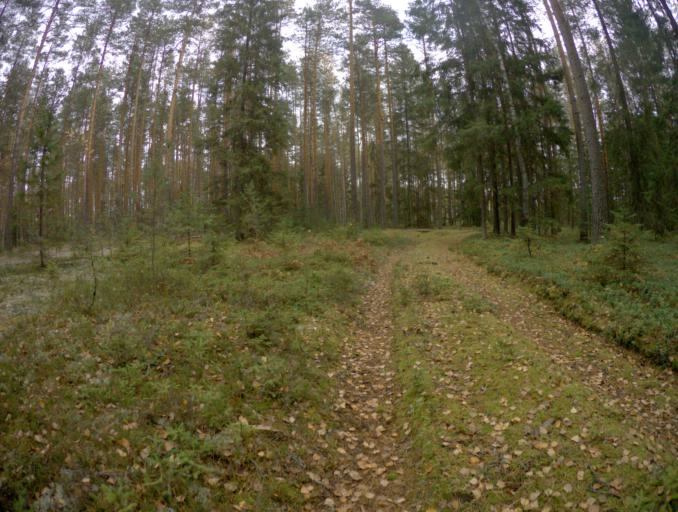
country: RU
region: Vladimir
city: Raduzhnyy
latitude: 55.9294
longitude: 40.3386
